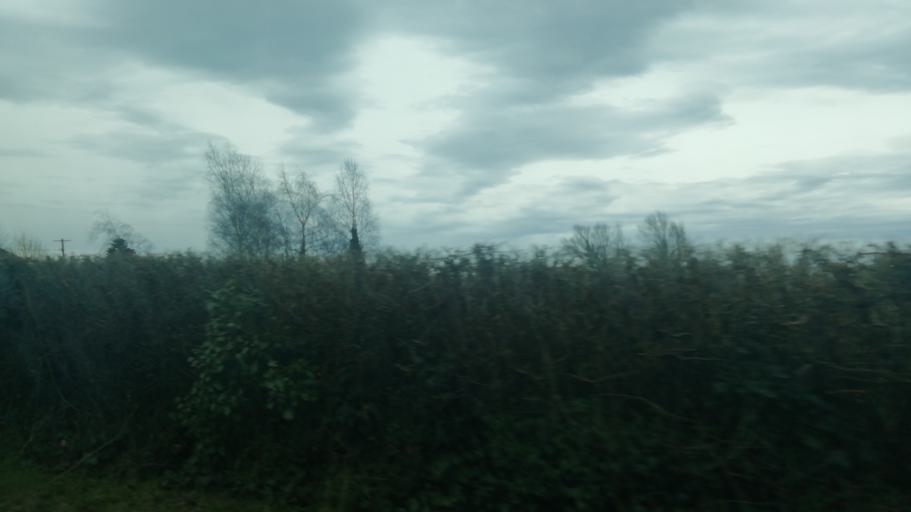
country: IE
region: Leinster
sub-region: Kildare
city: Clane
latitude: 53.3042
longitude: -6.6662
